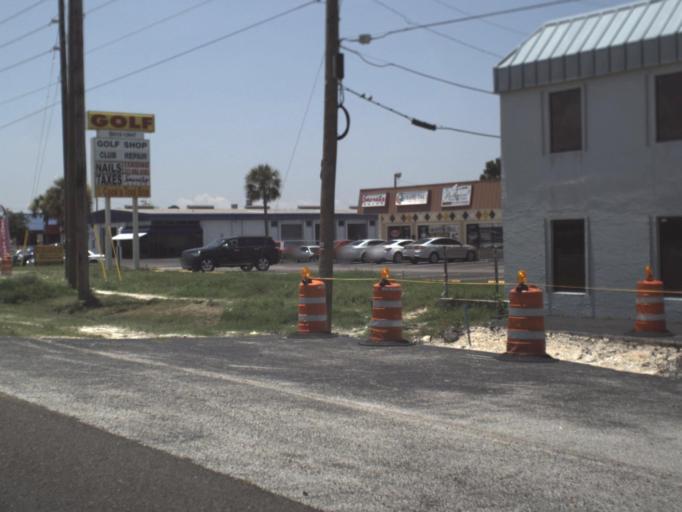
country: US
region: Florida
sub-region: Pasco County
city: Bayonet Point
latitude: 28.3416
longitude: -82.6994
